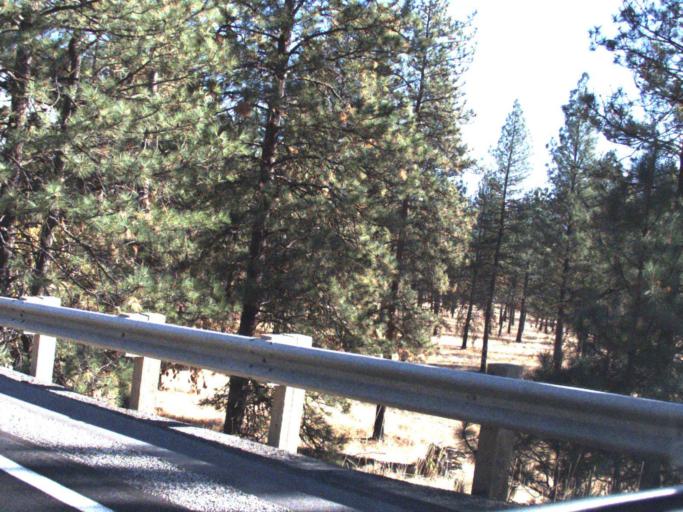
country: US
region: Washington
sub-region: Stevens County
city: Kettle Falls
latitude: 48.5879
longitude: -118.1493
